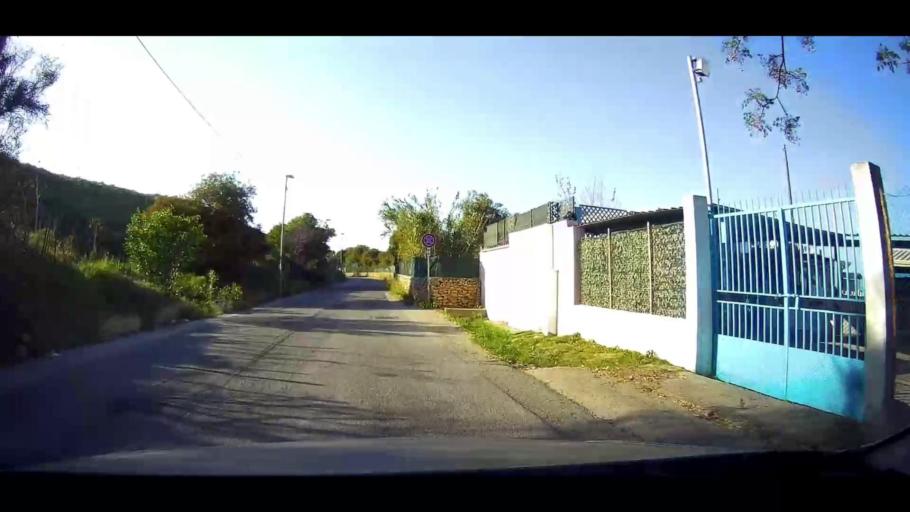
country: IT
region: Calabria
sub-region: Provincia di Crotone
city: Crotone
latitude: 39.0469
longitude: 17.1455
